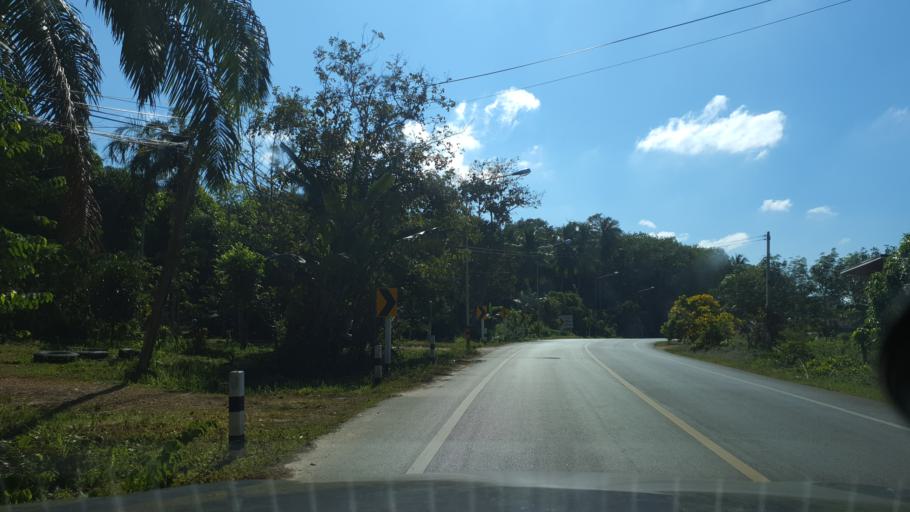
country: TH
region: Phangnga
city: Ban Ao Nang
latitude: 8.0709
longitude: 98.8081
